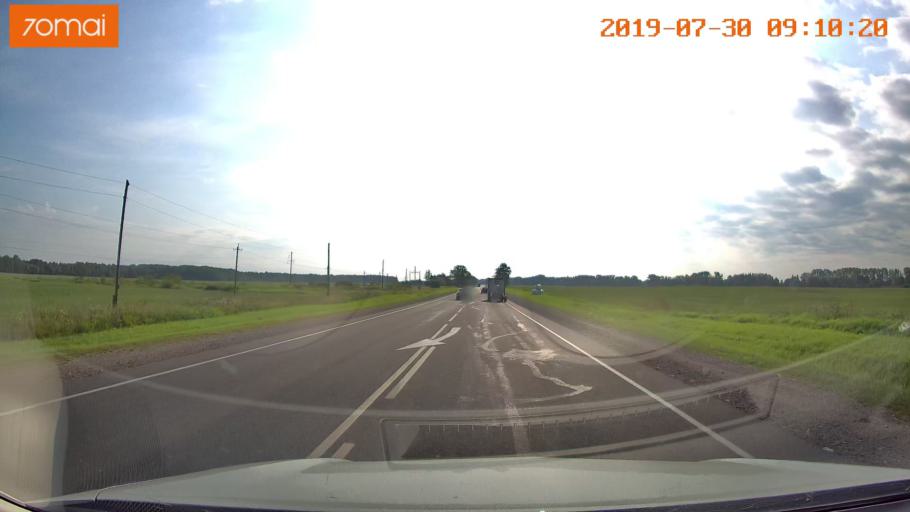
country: RU
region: Kaliningrad
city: Nesterov
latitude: 54.6120
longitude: 22.4249
